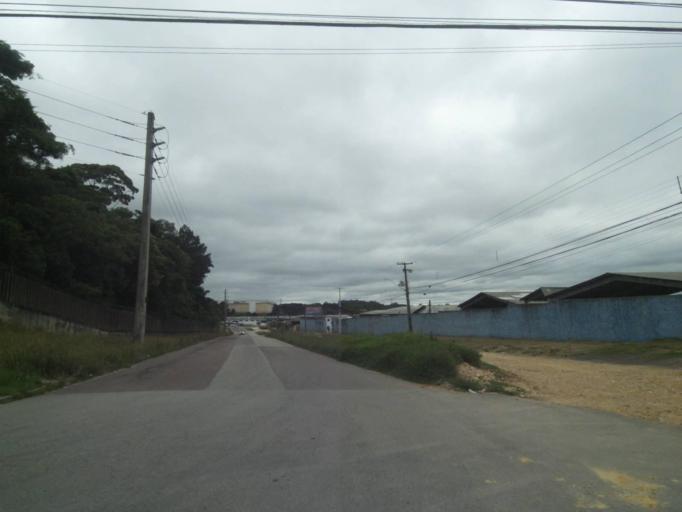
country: BR
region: Parana
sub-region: Araucaria
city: Araucaria
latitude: -25.5601
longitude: -49.3111
